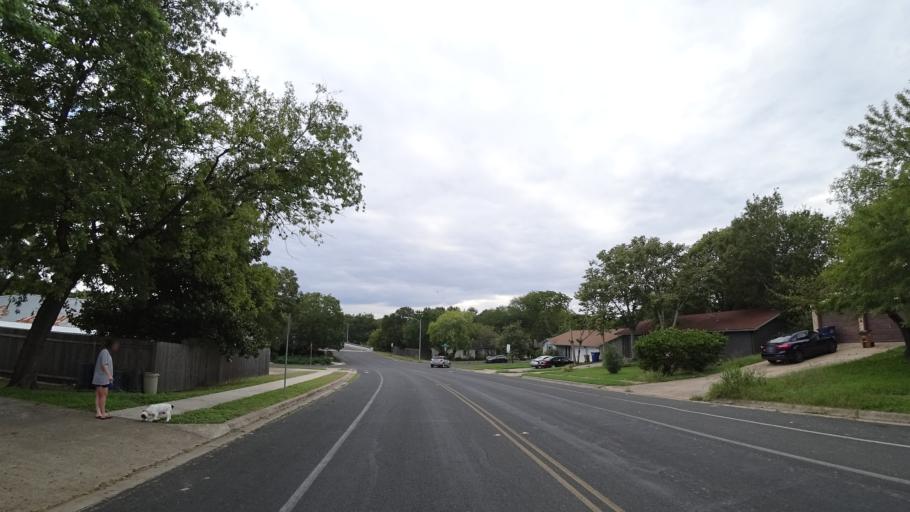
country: US
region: Texas
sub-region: Travis County
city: Rollingwood
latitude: 30.2157
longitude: -97.7854
